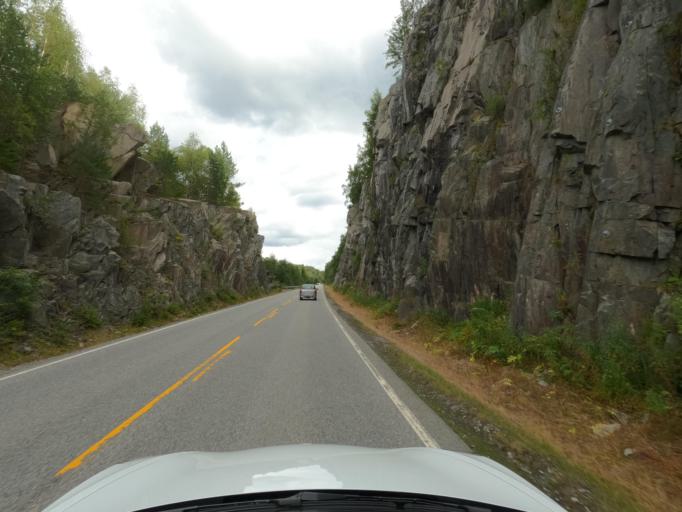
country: NO
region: Telemark
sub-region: Hjartdal
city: Sauland
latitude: 59.8316
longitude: 8.9724
